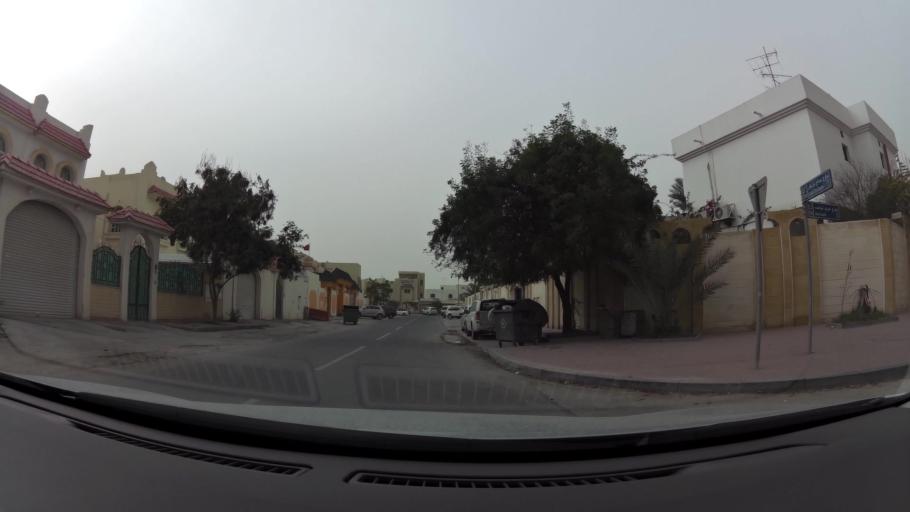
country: QA
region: Baladiyat ad Dawhah
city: Doha
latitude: 25.2514
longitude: 51.4896
